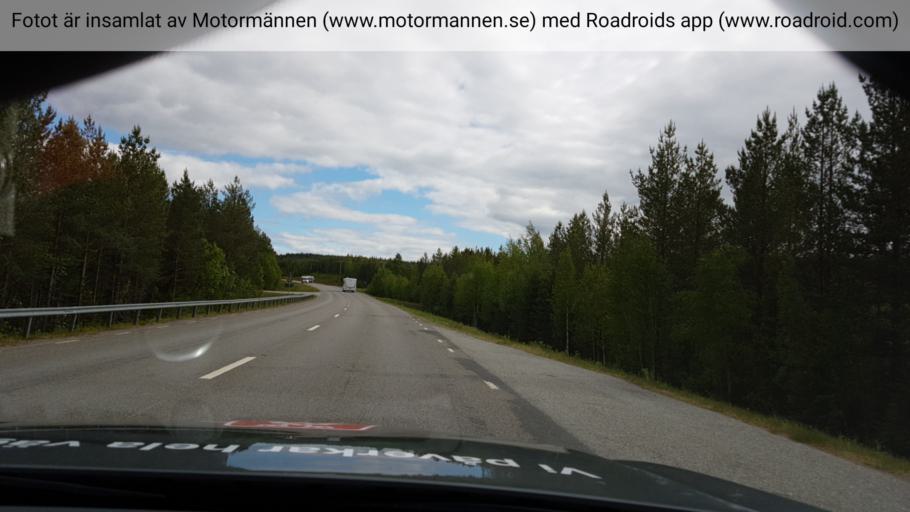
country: SE
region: Jaemtland
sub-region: Stroemsunds Kommun
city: Stroemsund
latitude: 64.2400
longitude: 15.4530
